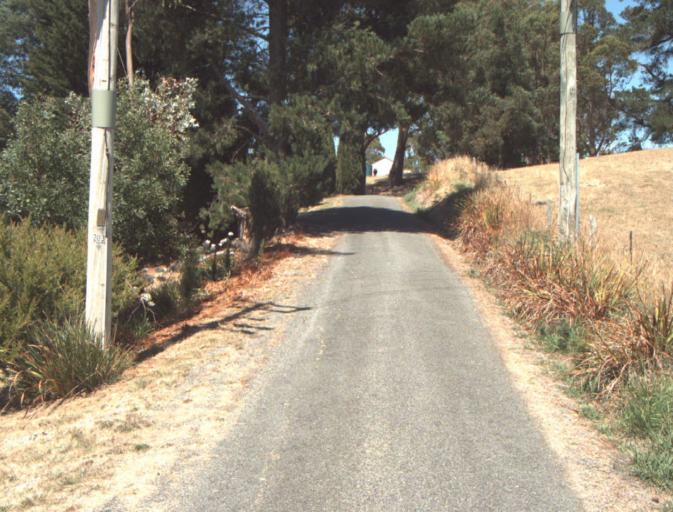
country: AU
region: Tasmania
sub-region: Launceston
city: Mayfield
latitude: -41.2579
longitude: 147.1444
